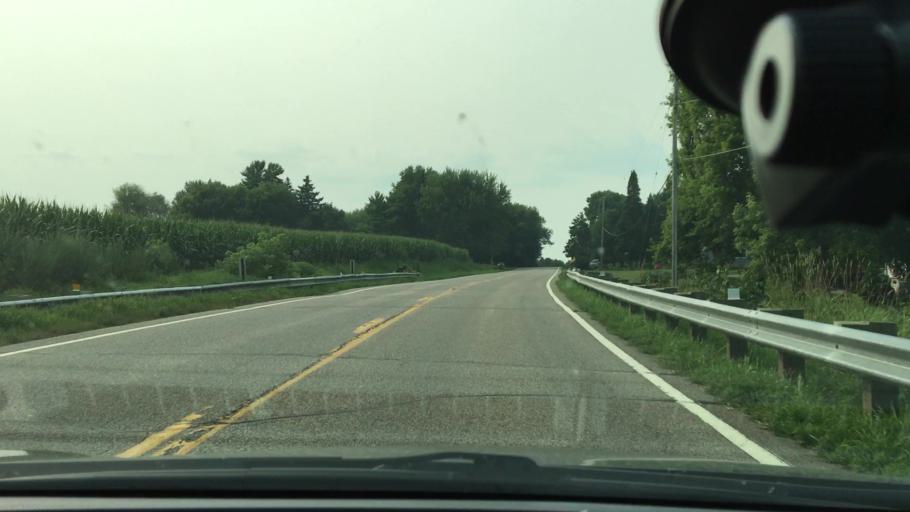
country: US
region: Minnesota
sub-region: Hennepin County
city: Dayton
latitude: 45.2254
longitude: -93.4891
